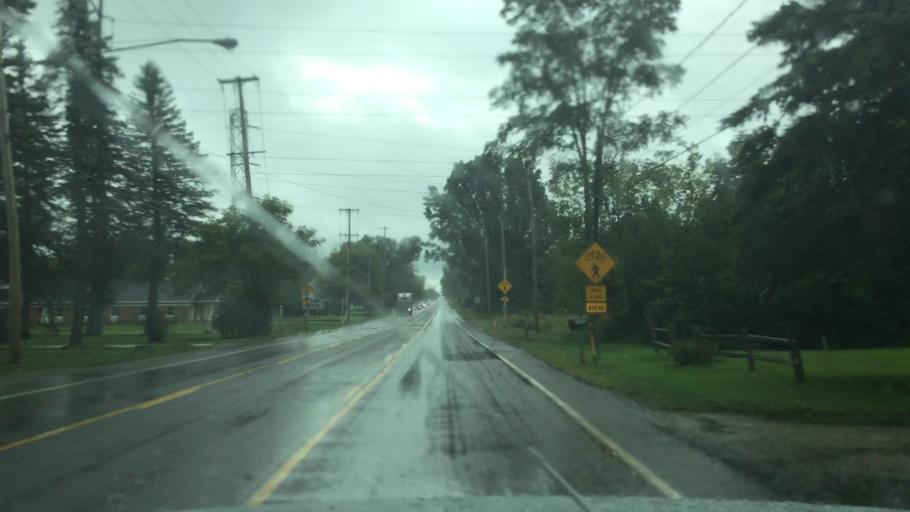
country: US
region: Michigan
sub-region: Eaton County
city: Dimondale
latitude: 42.6771
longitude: -84.6031
